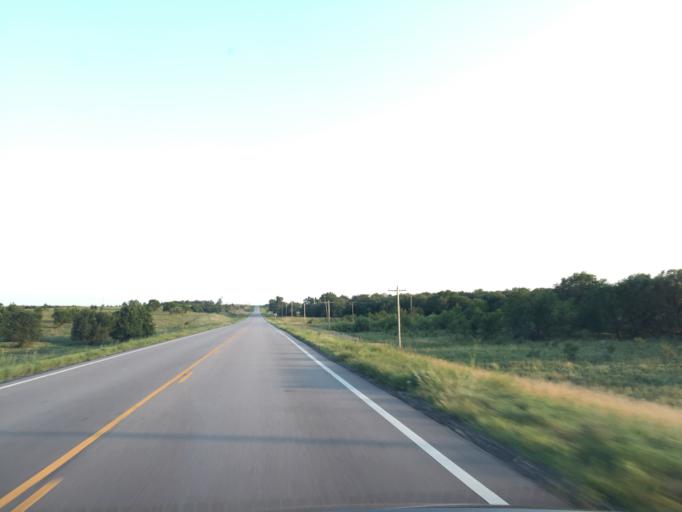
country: US
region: Kansas
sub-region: Ellsworth County
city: Ellsworth
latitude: 38.5845
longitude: -98.2017
